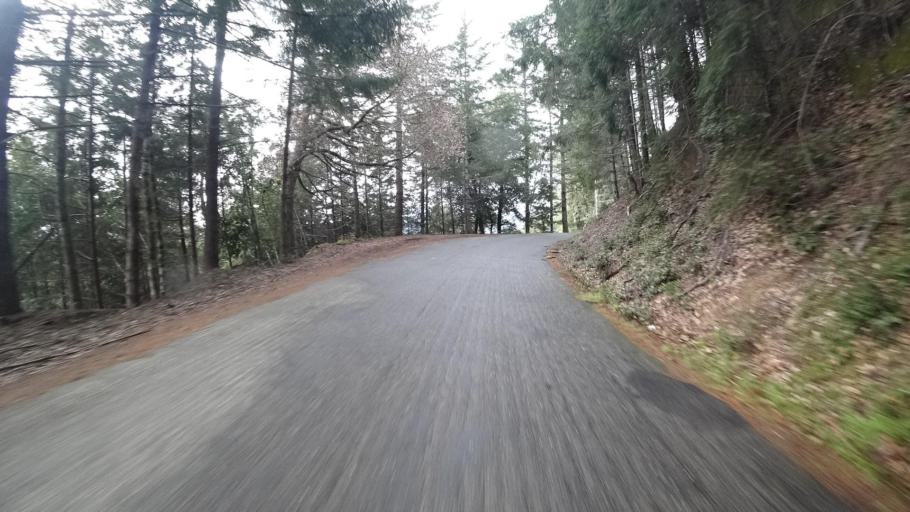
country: US
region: California
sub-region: Humboldt County
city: Redway
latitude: 40.2675
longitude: -123.7673
